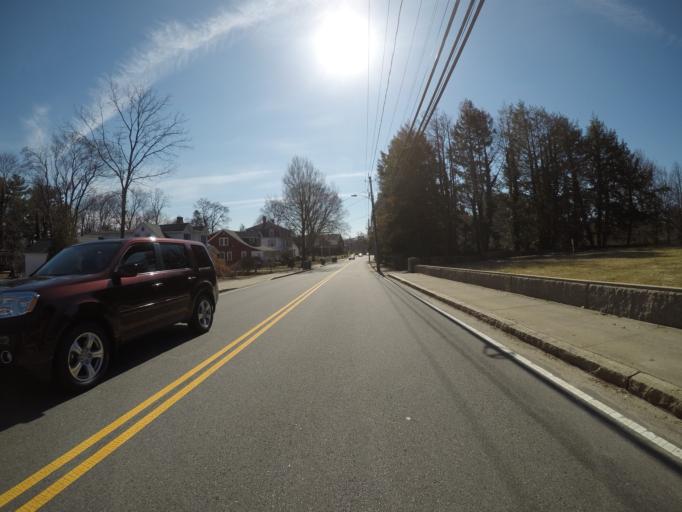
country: US
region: Massachusetts
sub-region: Bristol County
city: Easton
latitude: 42.0705
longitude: -71.1060
